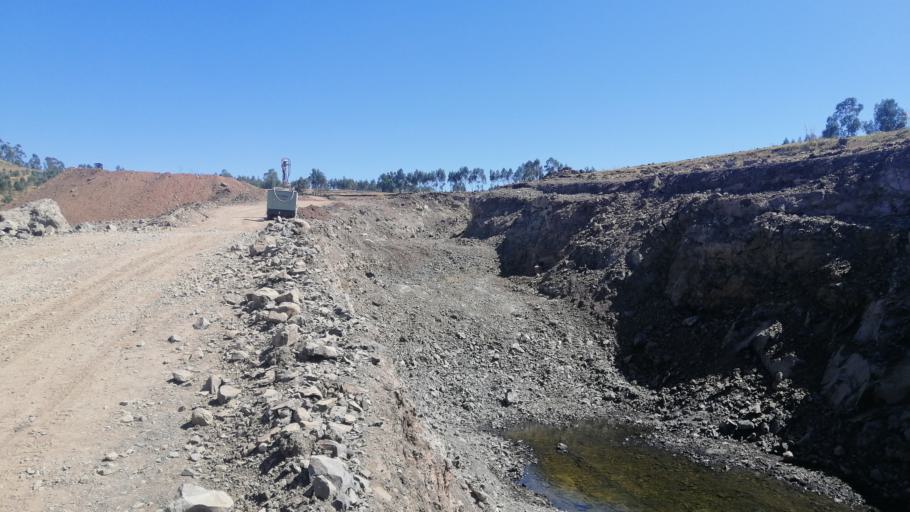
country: ET
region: Amhara
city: Debre Tabor
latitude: 11.4199
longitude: 38.2135
